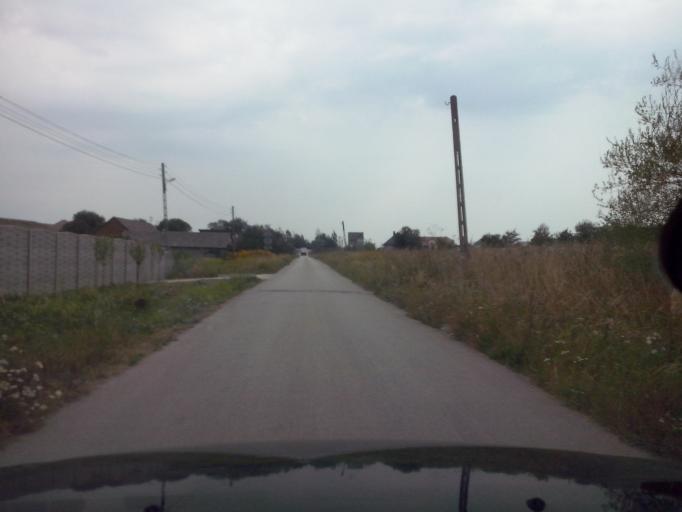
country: PL
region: Swietokrzyskie
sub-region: Powiat kielecki
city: Brzeziny
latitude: 50.7815
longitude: 20.5563
